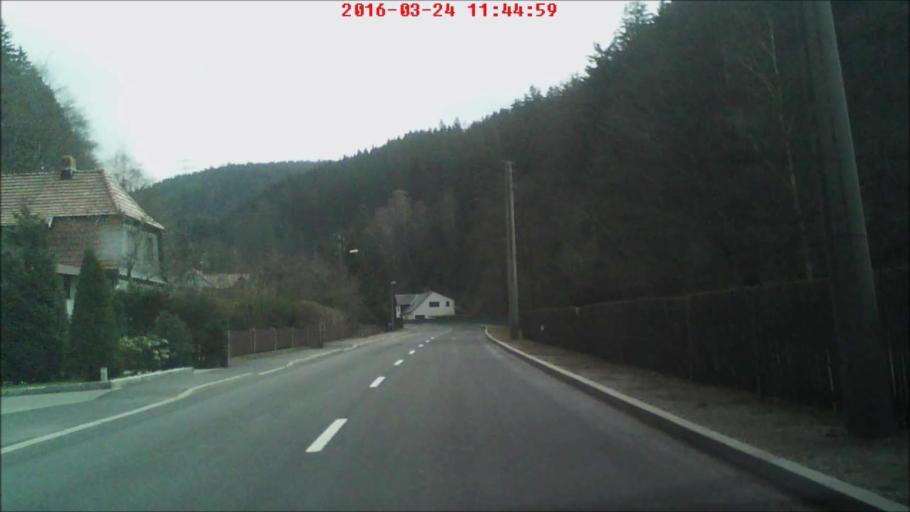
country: DE
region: Thuringia
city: Bachfeld
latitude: 50.4587
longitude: 10.9854
